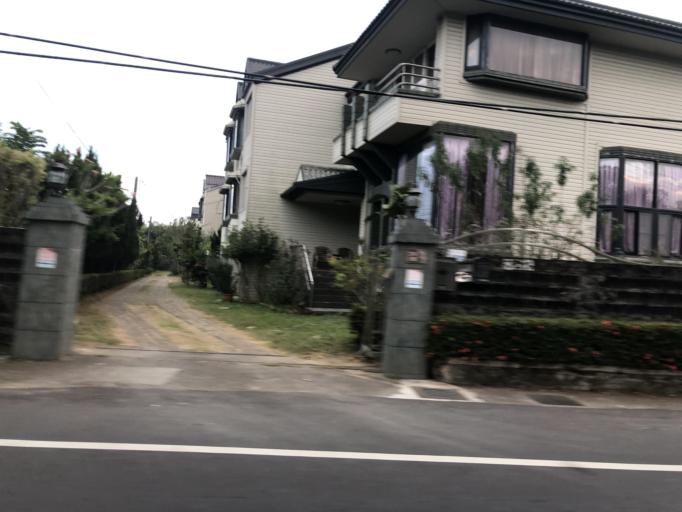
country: TW
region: Taiwan
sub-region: Tainan
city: Tainan
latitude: 23.0256
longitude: 120.3429
